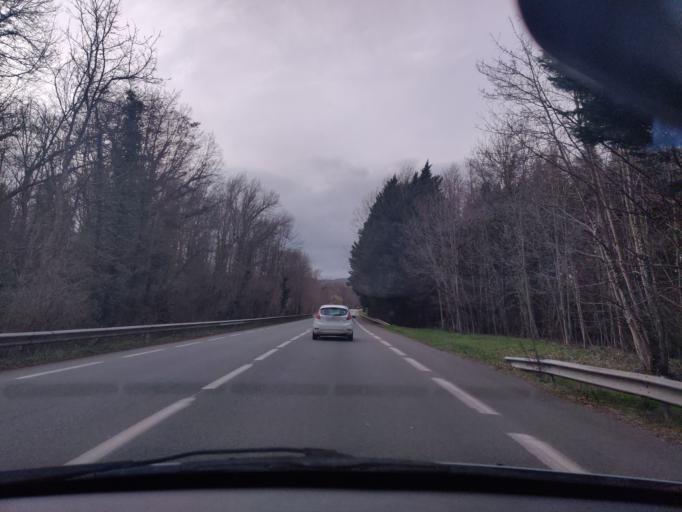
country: FR
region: Auvergne
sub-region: Departement du Puy-de-Dome
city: Marsat
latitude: 45.8823
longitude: 3.0873
